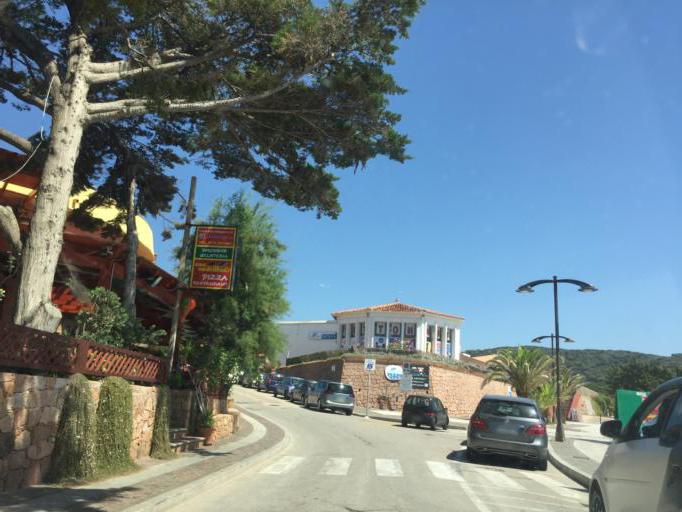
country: IT
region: Sardinia
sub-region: Provincia di Olbia-Tempio
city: Trinita d'Agultu
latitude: 41.0121
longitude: 8.8762
